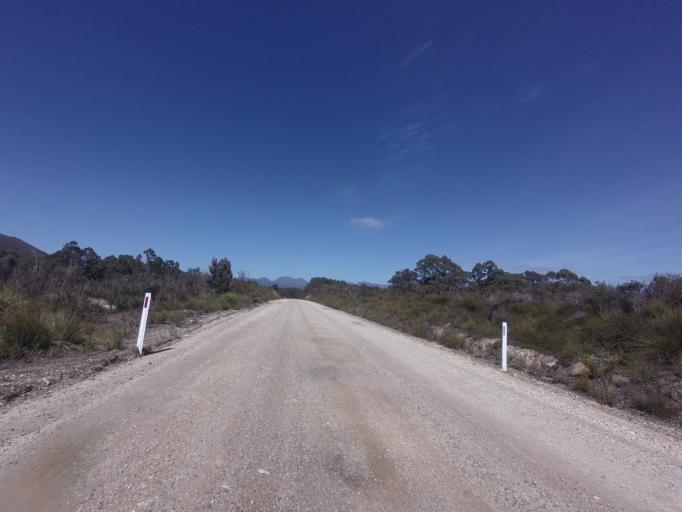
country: AU
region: Tasmania
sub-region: Huon Valley
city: Geeveston
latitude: -43.0248
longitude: 146.3551
